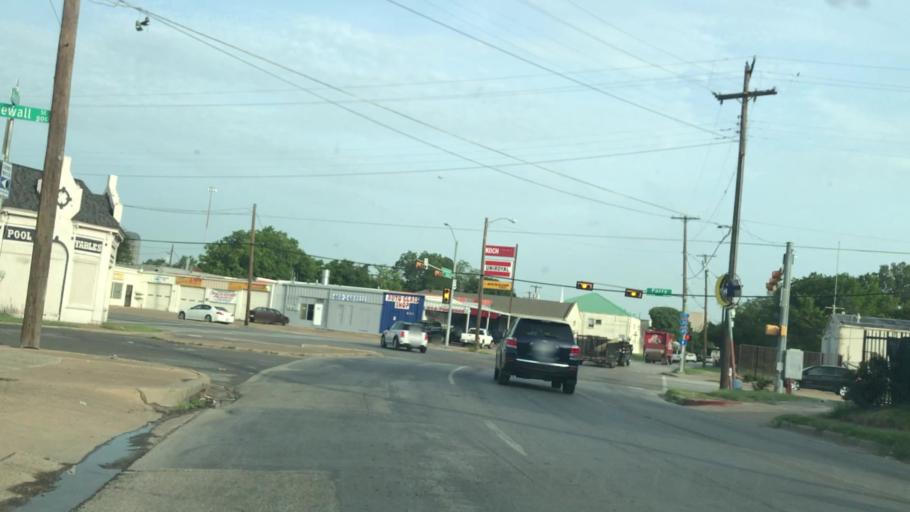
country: US
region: Texas
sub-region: Dallas County
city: Dallas
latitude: 32.7851
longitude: -96.7632
